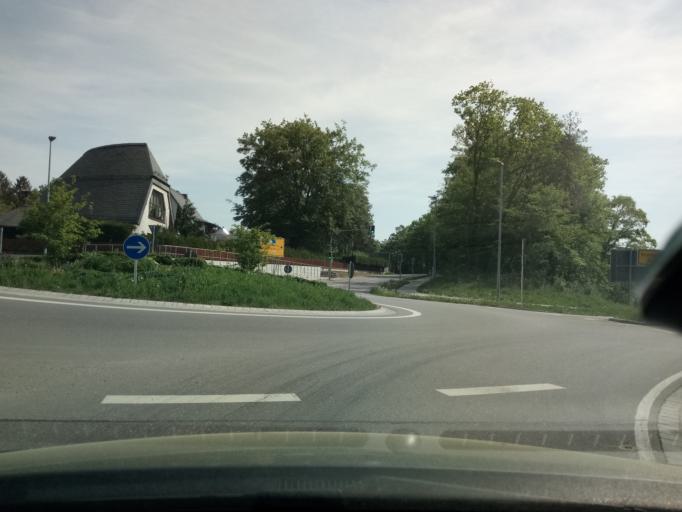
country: DE
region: Bavaria
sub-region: Upper Bavaria
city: Waldkraiburg
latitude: 48.1969
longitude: 12.3960
